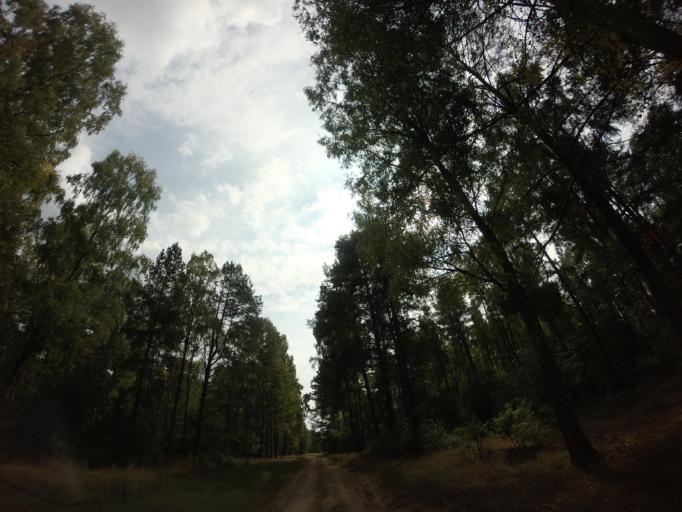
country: PL
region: West Pomeranian Voivodeship
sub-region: Powiat drawski
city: Drawsko Pomorskie
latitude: 53.4652
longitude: 15.7332
